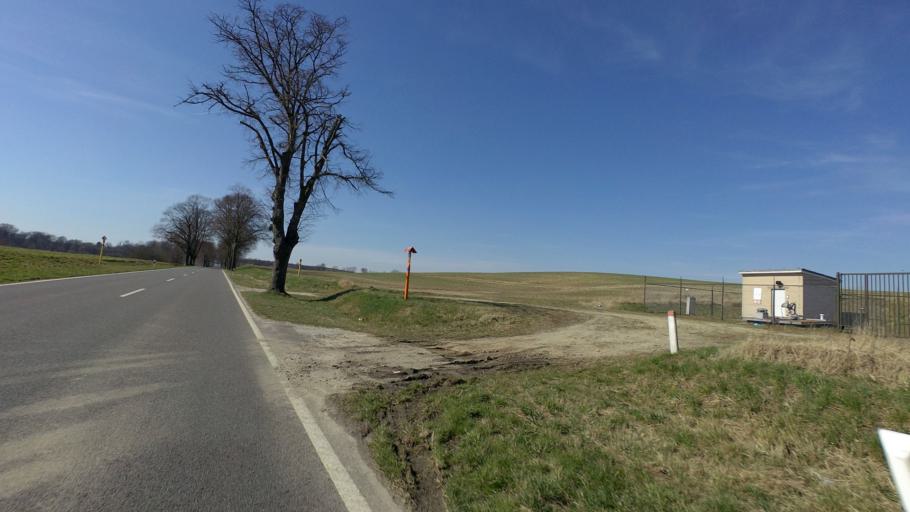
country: DE
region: Brandenburg
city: Protzel
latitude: 52.6354
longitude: 14.0029
